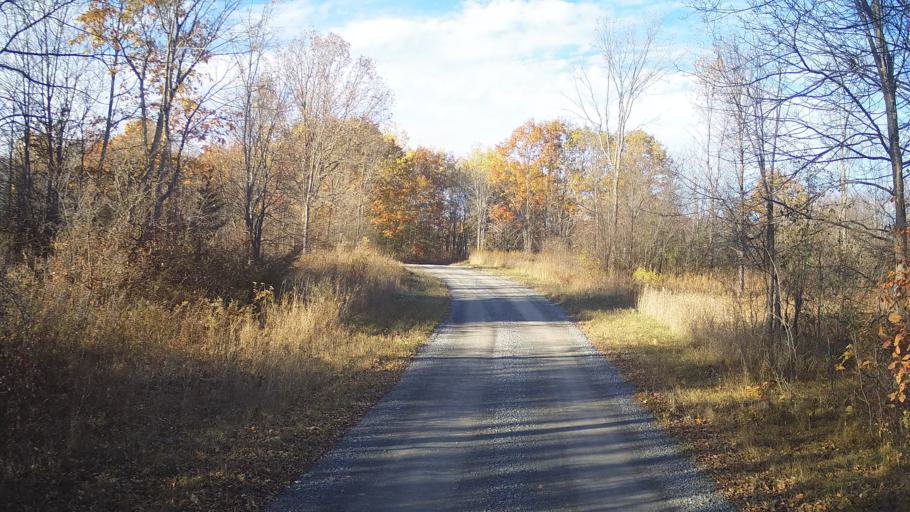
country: CA
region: Ontario
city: Perth
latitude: 44.7241
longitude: -76.4395
